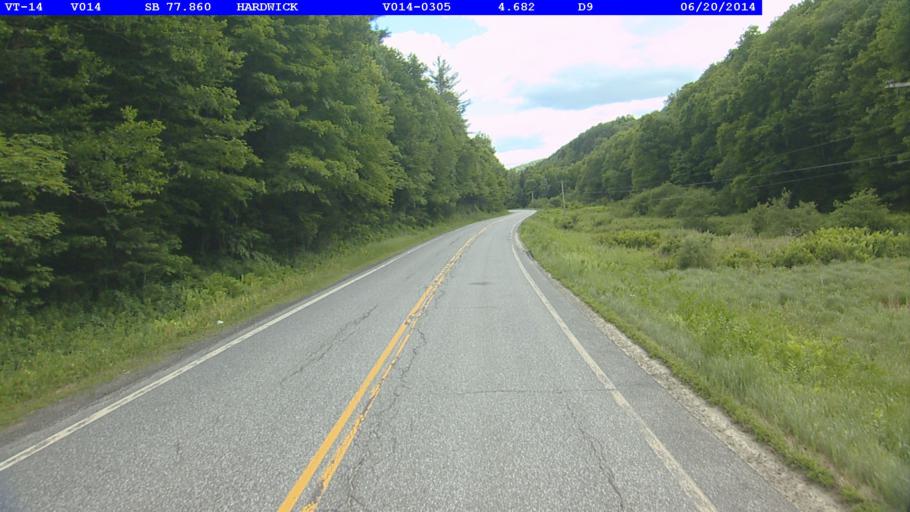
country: US
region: Vermont
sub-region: Caledonia County
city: Hardwick
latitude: 44.5609
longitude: -72.3679
